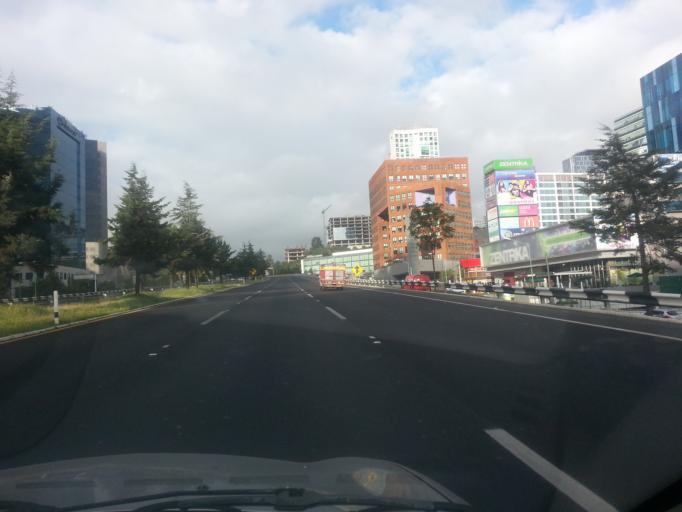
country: MX
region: Mexico City
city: Cuajimalpa
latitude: 19.3594
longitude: -99.2737
